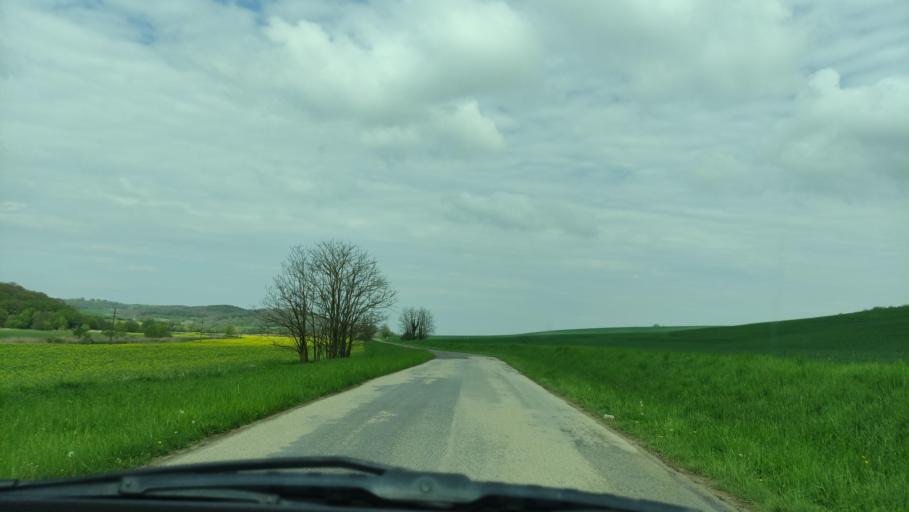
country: HU
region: Baranya
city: Magocs
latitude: 46.2832
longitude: 18.2034
